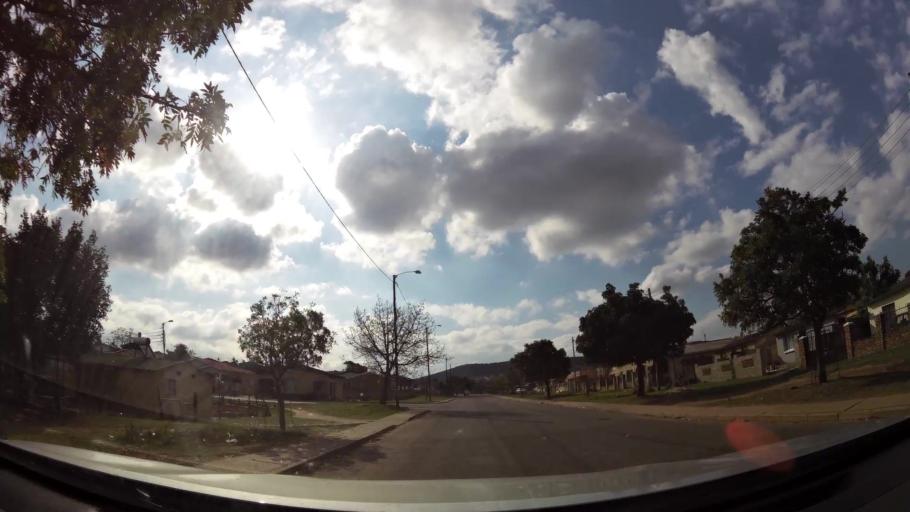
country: ZA
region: Eastern Cape
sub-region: Nelson Mandela Bay Metropolitan Municipality
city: Uitenhage
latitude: -33.7381
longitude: 25.3813
